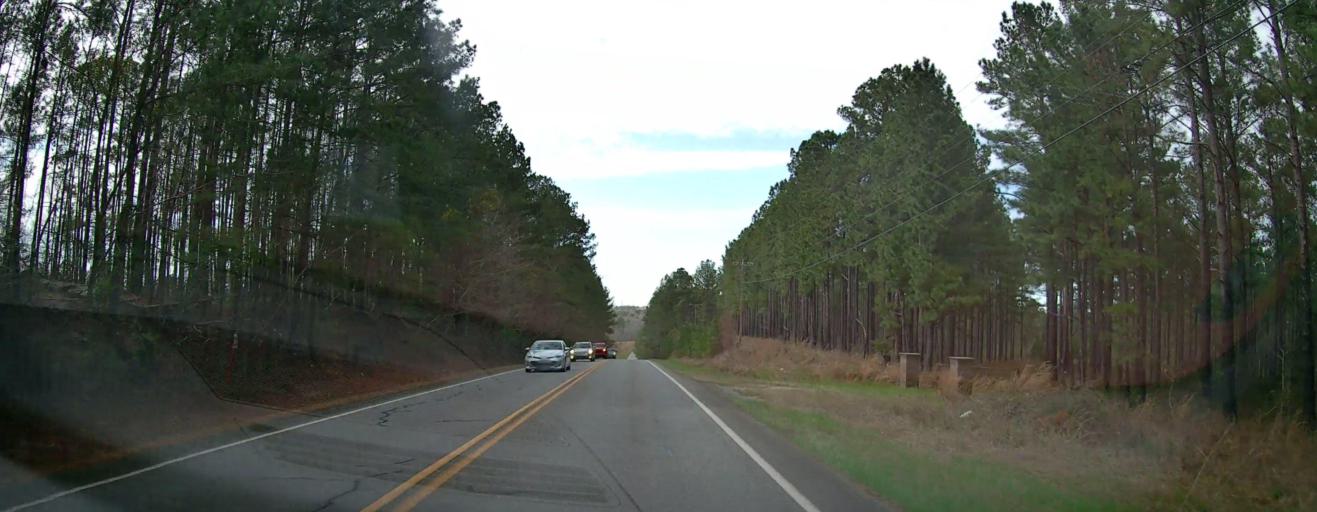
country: US
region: Georgia
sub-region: Jones County
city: Gray
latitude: 32.9957
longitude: -83.6888
